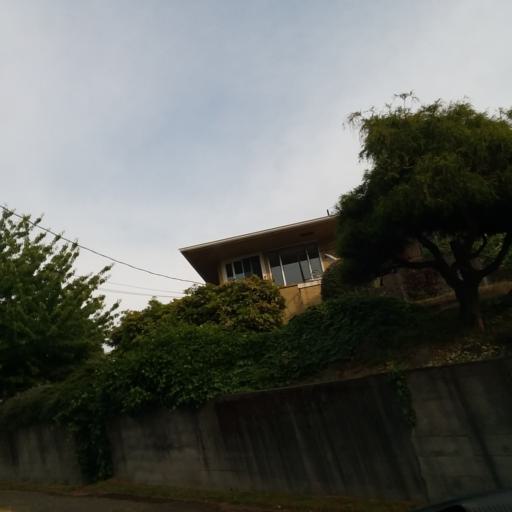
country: US
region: Washington
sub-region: King County
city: Seattle
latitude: 47.5790
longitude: -122.4018
